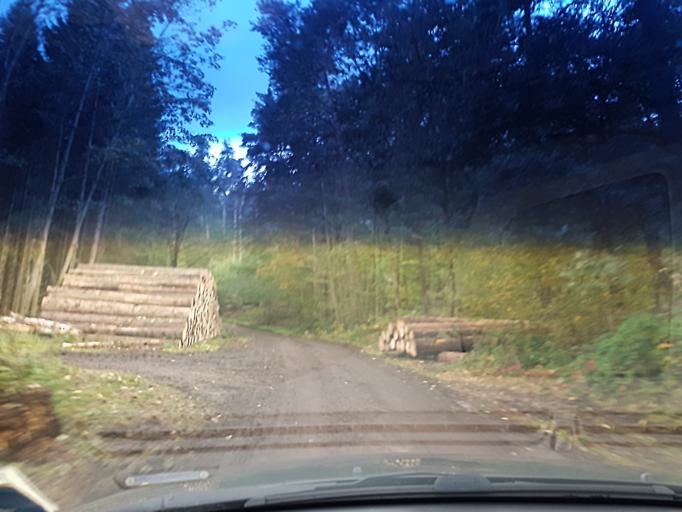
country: DE
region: Bavaria
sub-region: Regierungsbezirk Mittelfranken
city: Markt Taschendorf
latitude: 49.7625
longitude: 10.5370
